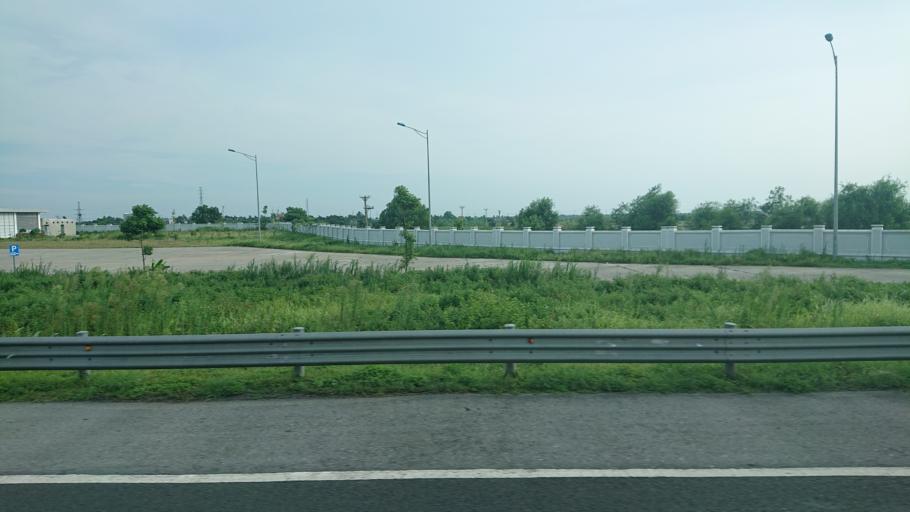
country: VN
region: Hai Phong
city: An Lao
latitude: 20.7942
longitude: 106.5468
